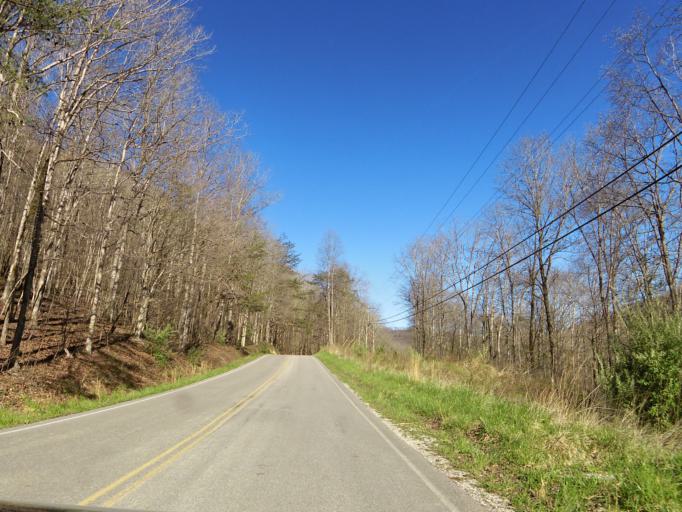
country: US
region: Tennessee
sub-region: Scott County
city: Huntsville
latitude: 36.2972
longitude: -84.3814
